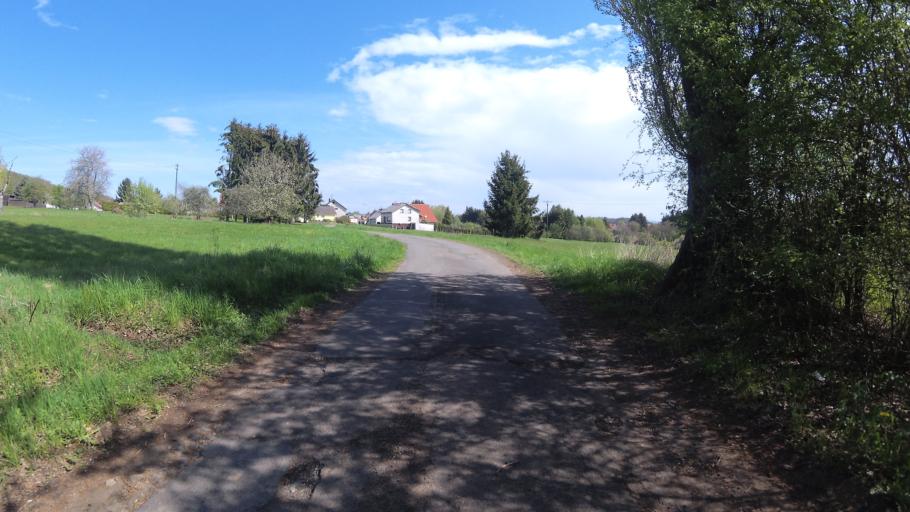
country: DE
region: Saarland
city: Marpingen
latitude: 49.4672
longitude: 7.1009
